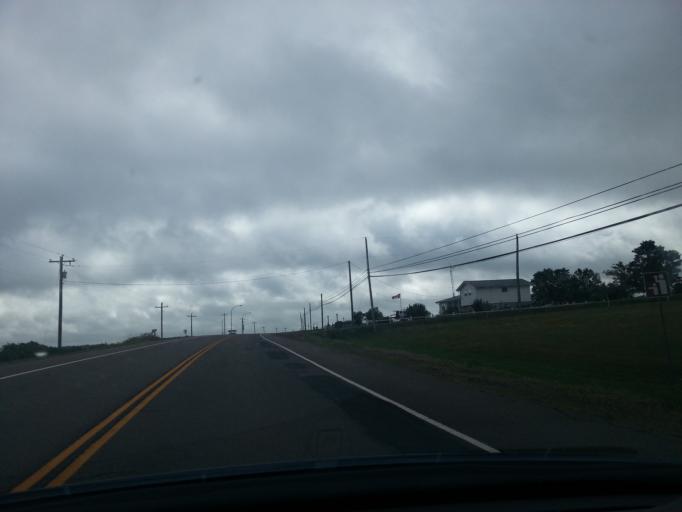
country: CA
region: Prince Edward Island
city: Montague
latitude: 46.4155
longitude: -62.6196
